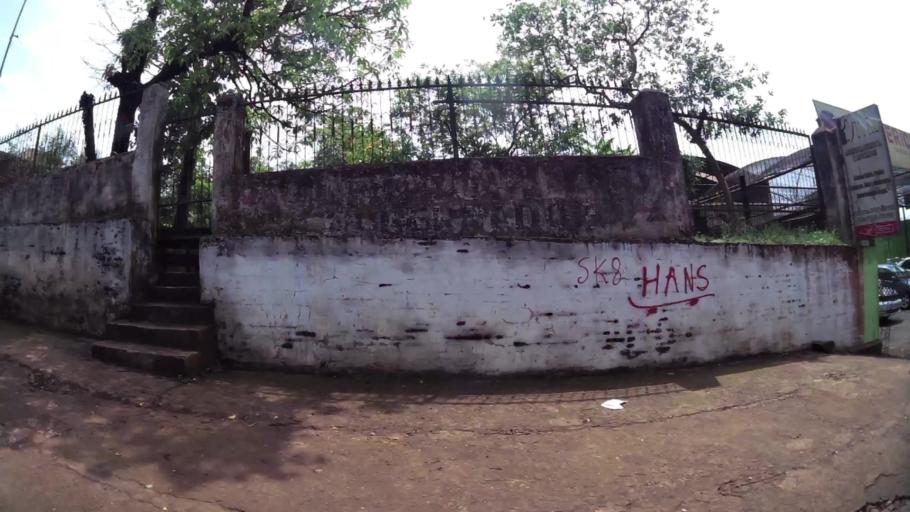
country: PY
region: Alto Parana
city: Ciudad del Este
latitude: -25.5099
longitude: -54.6608
